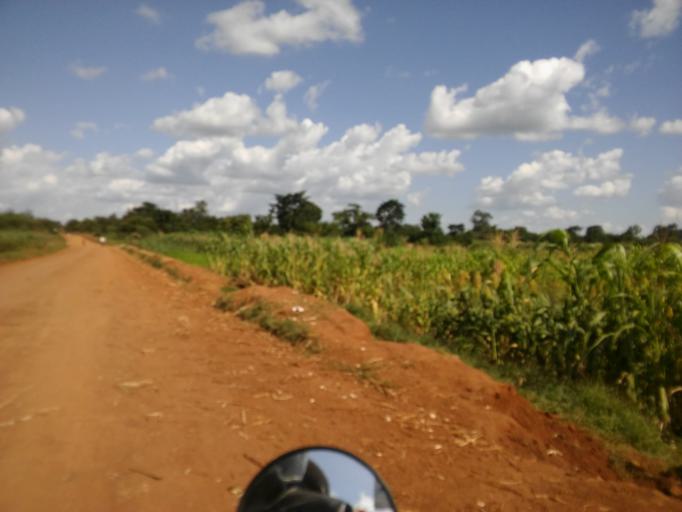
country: UG
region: Eastern Region
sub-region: Pallisa District
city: Pallisa
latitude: 1.1329
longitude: 33.7297
